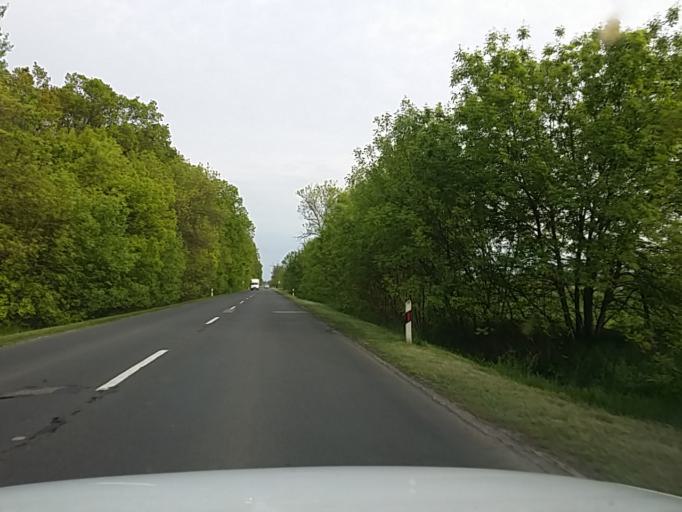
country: HU
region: Pest
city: Szentlorinckata
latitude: 47.5714
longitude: 19.7698
